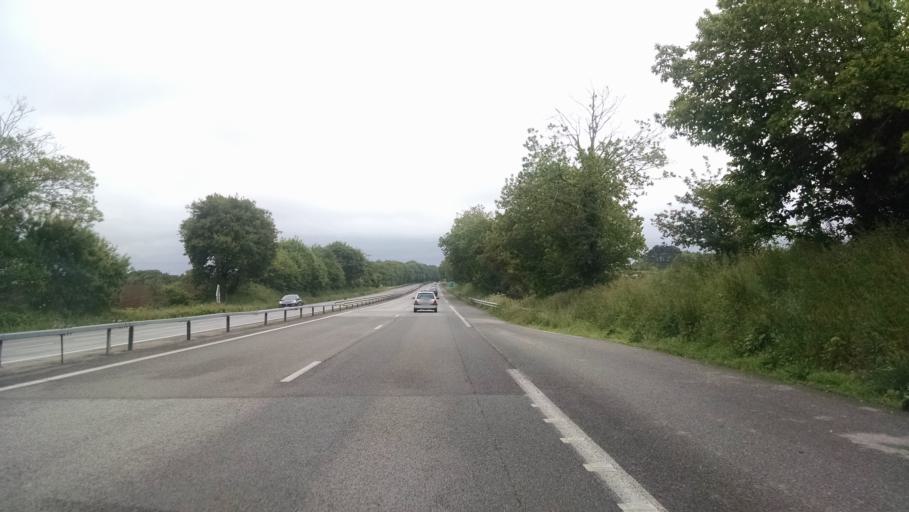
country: FR
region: Brittany
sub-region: Departement du Finistere
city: Melgven
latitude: 47.9216
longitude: -3.8880
